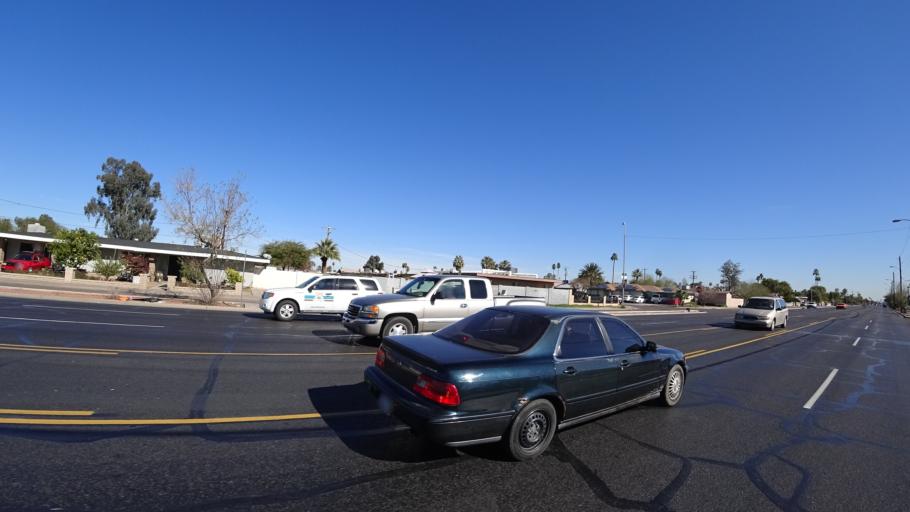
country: US
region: Arizona
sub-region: Maricopa County
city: Glendale
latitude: 33.4950
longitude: -112.1828
